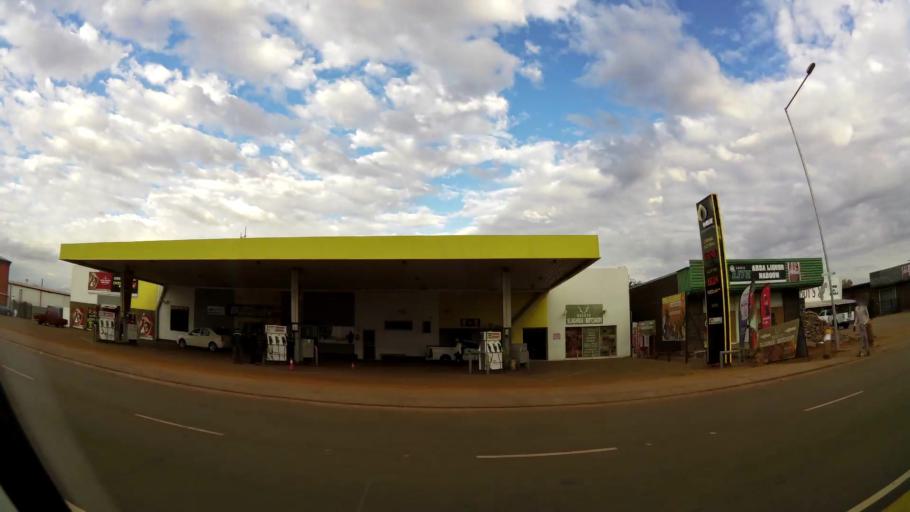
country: ZA
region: Limpopo
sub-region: Waterberg District Municipality
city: Modimolle
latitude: -24.5176
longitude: 28.7163
